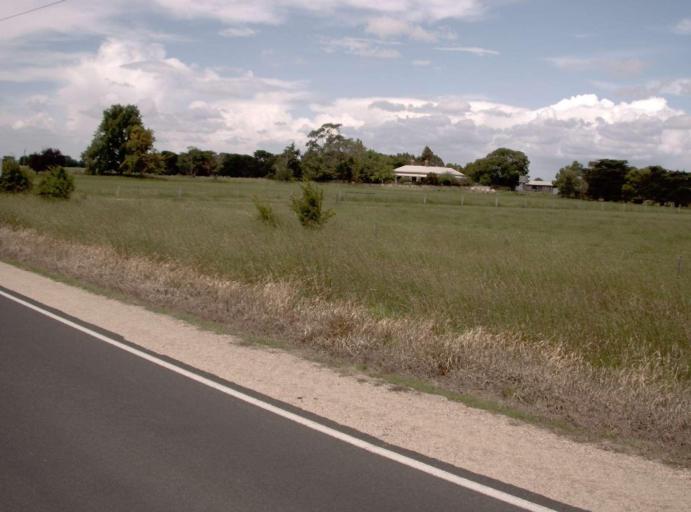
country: AU
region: Victoria
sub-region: Wellington
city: Sale
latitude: -38.0261
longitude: 147.0130
